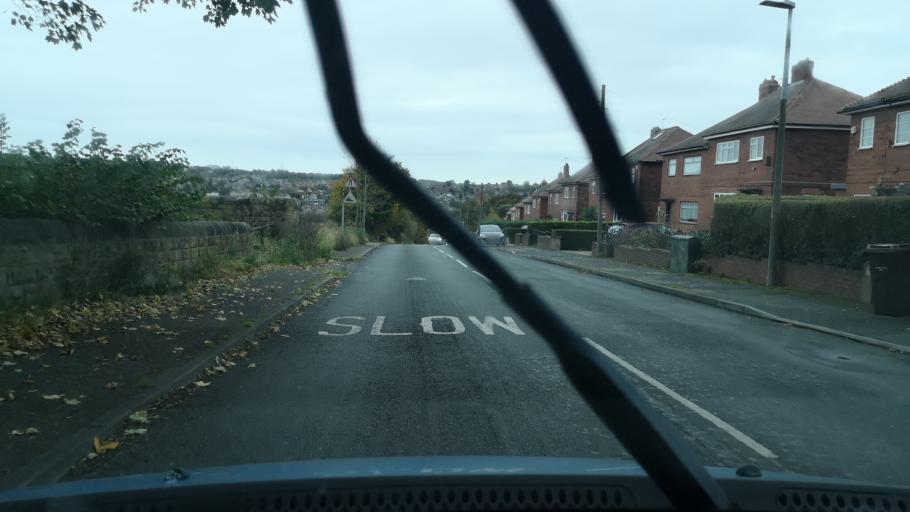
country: GB
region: England
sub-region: Kirklees
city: Heckmondwike
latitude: 53.7227
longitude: -1.6635
